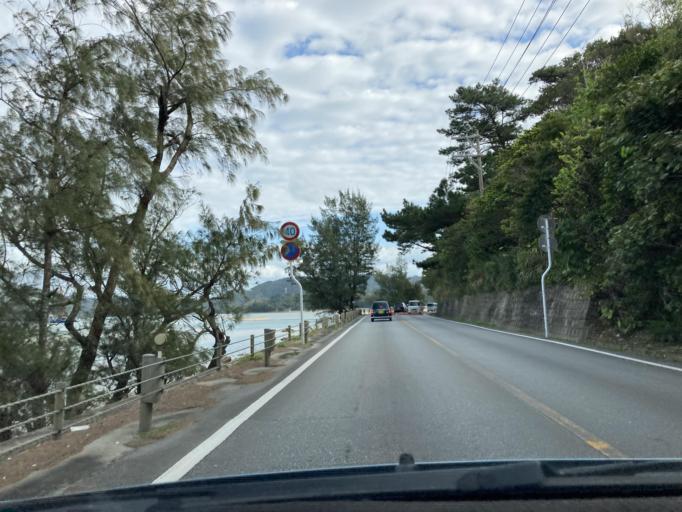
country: JP
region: Okinawa
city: Nago
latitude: 26.6383
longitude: 128.0030
